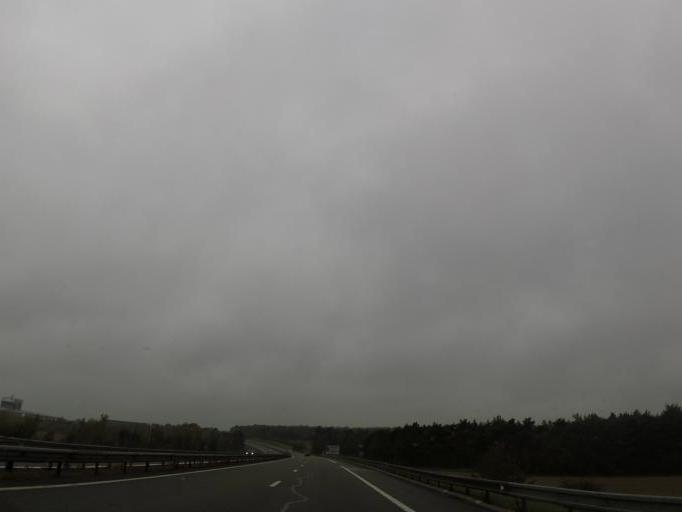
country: FR
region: Champagne-Ardenne
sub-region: Departement de la Marne
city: Fagnieres
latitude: 49.0375
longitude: 4.3502
